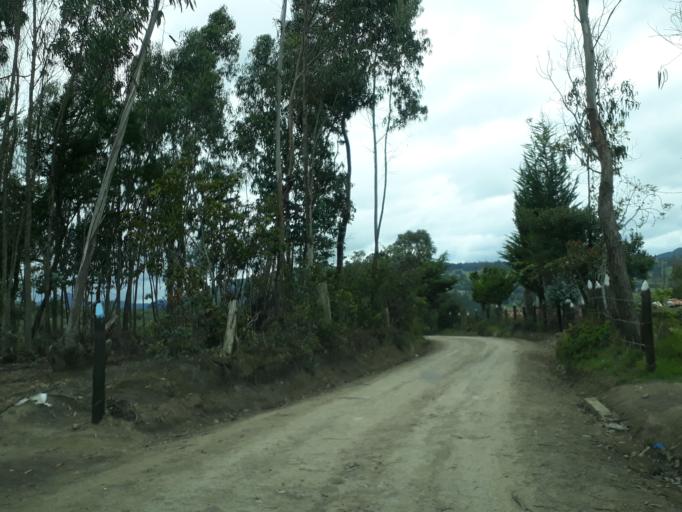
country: CO
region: Boyaca
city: Chiquinquira
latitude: 5.5623
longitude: -73.8118
